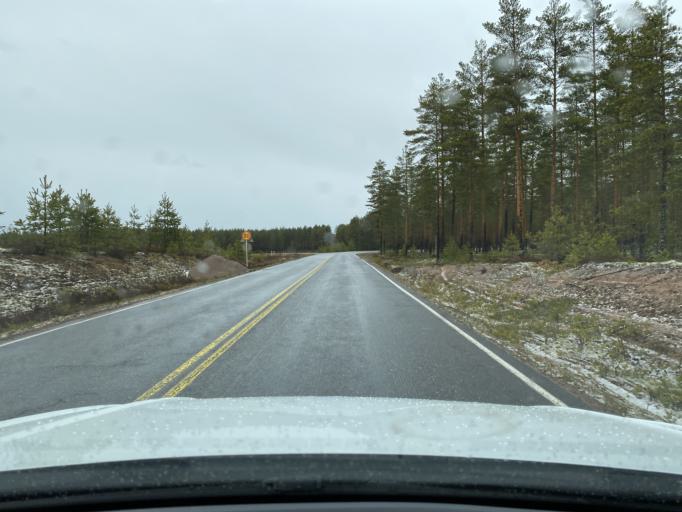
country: FI
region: Satakunta
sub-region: Pori
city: Vampula
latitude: 60.9631
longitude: 22.6758
